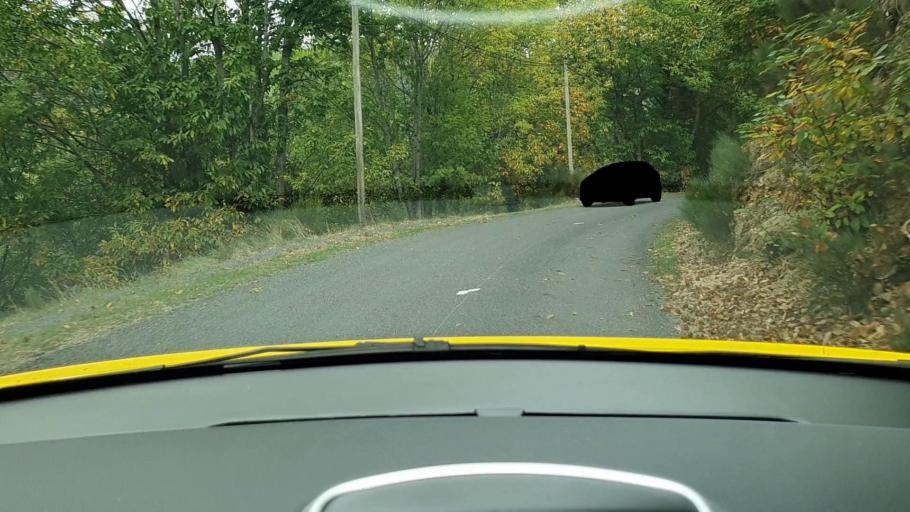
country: FR
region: Languedoc-Roussillon
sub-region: Departement de la Lozere
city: Meyrueis
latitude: 44.0617
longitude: 3.4284
